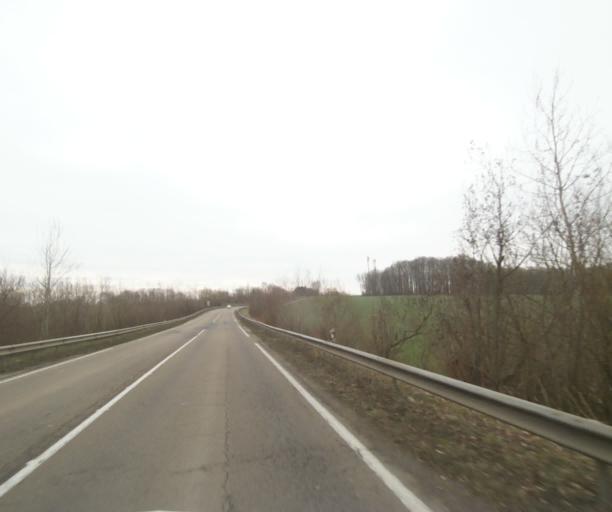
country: FR
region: Champagne-Ardenne
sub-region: Departement de la Haute-Marne
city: Bienville
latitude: 48.5791
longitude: 5.0323
